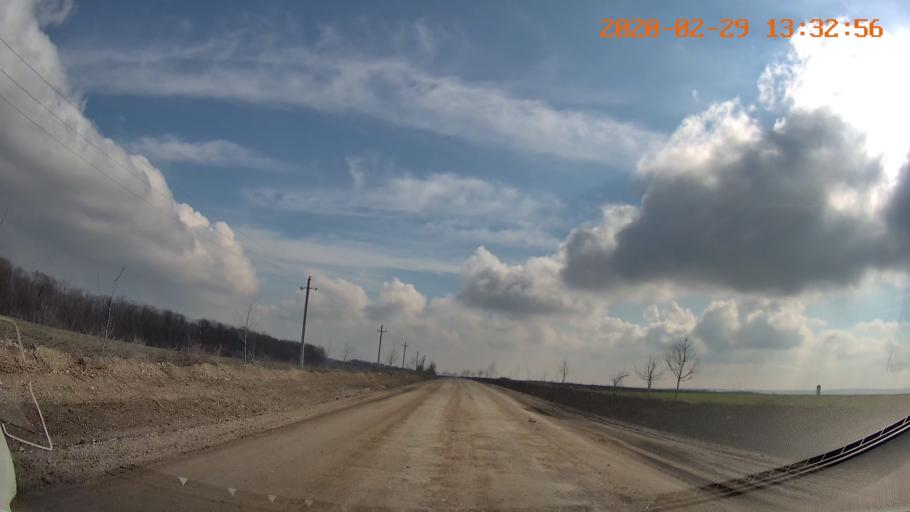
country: MD
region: Telenesti
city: Camenca
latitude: 47.8765
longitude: 28.6129
